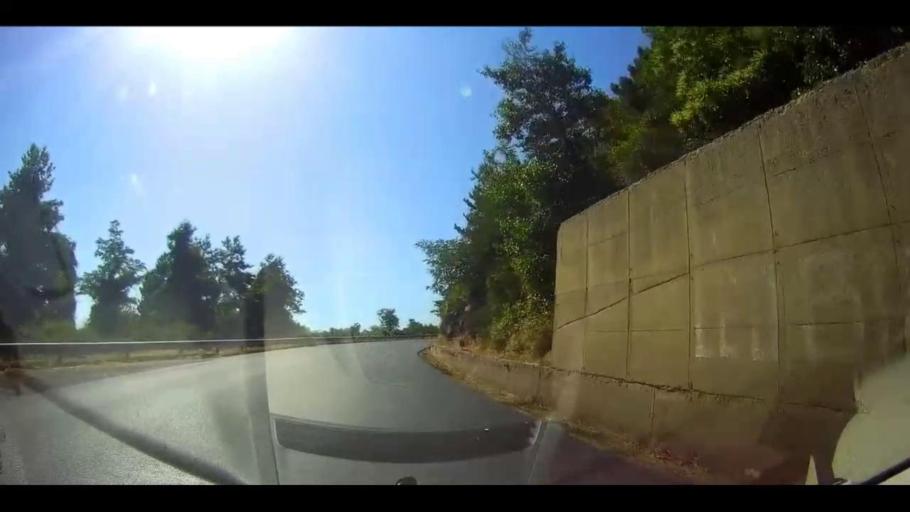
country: IT
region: Calabria
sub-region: Provincia di Cosenza
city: Celico
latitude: 39.3200
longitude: 16.3697
